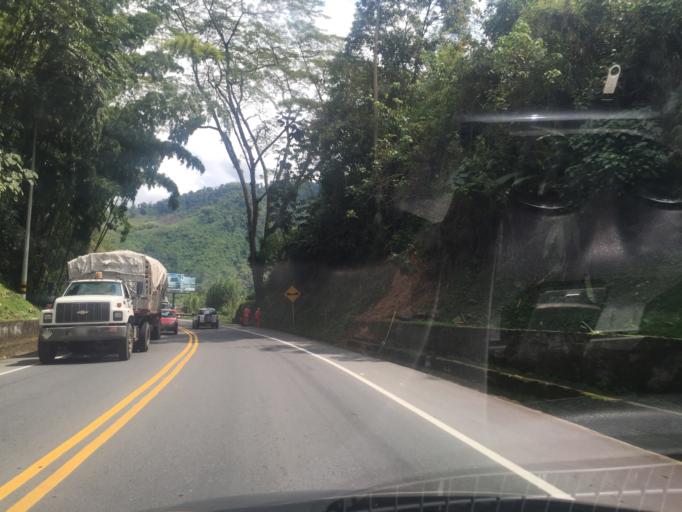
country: CO
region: Caldas
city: Chinchina
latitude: 4.9941
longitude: -75.6051
